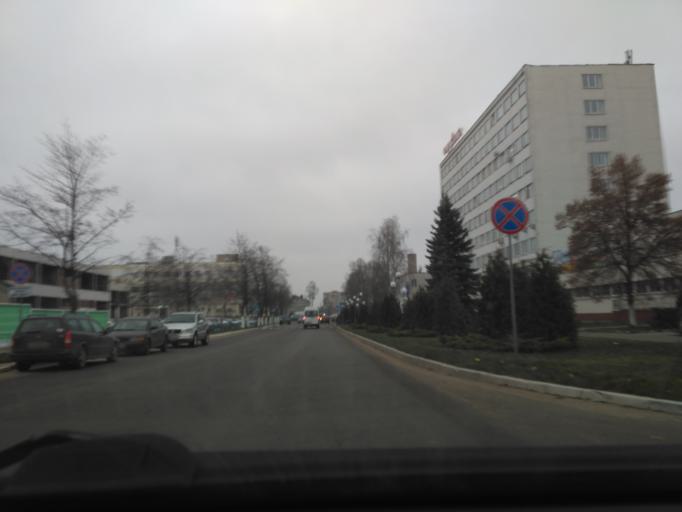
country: BY
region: Minsk
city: Horad Barysaw
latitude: 54.2118
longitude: 28.4909
